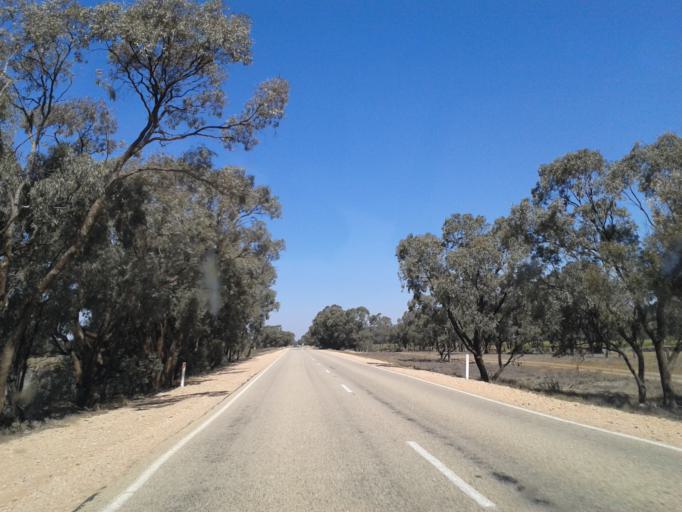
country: AU
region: Victoria
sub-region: Swan Hill
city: Swan Hill
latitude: -35.0138
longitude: 143.3111
